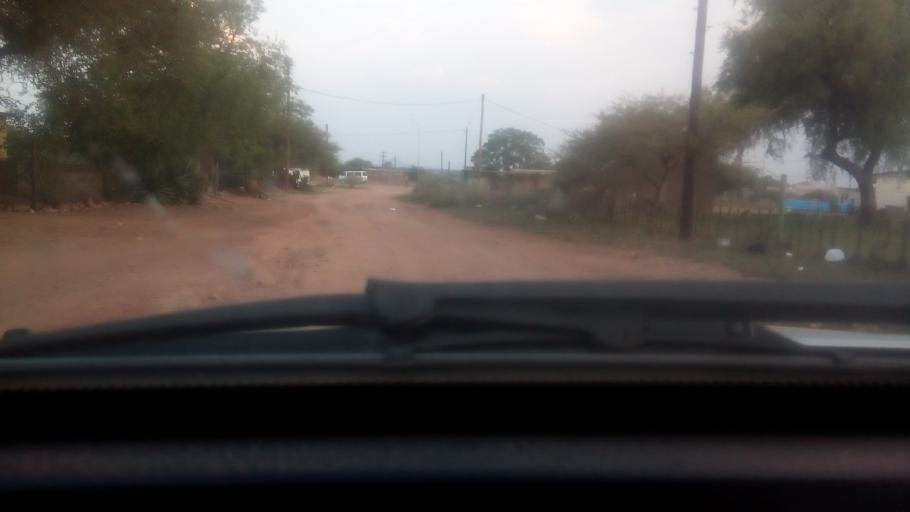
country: BW
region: Kgatleng
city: Bokaa
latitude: -24.4275
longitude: 26.0203
